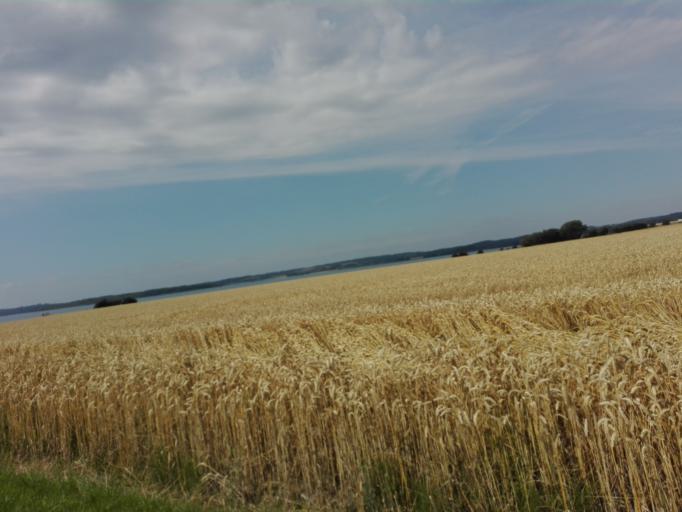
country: DK
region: Central Jutland
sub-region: Hedensted Kommune
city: Juelsminde
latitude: 55.8545
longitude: 10.0481
